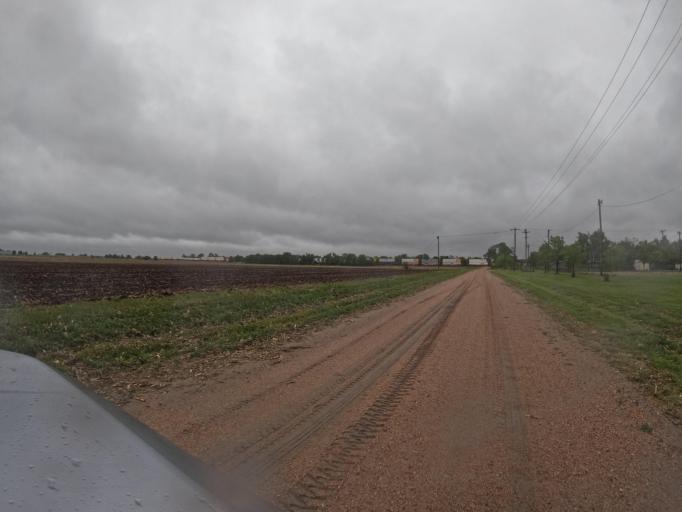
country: US
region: Nebraska
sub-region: Clay County
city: Harvard
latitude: 40.6145
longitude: -98.1027
